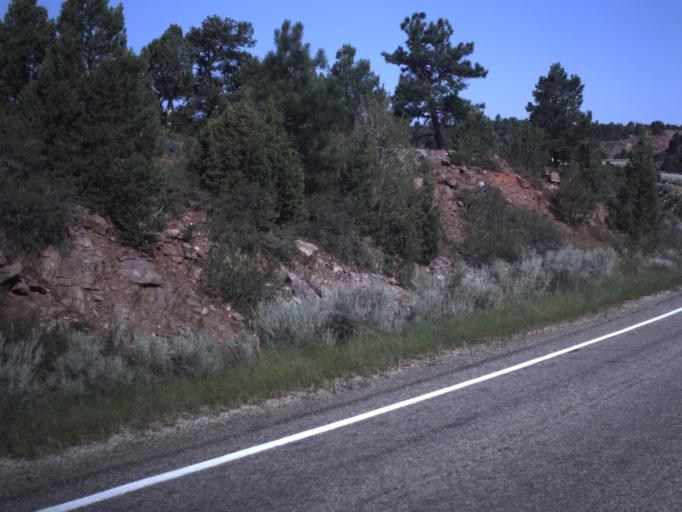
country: US
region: Utah
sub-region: Daggett County
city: Manila
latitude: 40.9201
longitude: -109.4152
